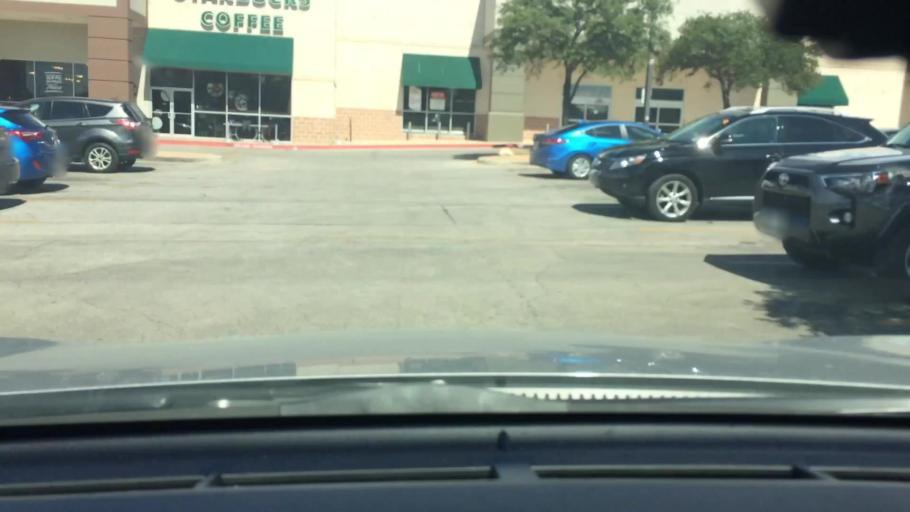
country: US
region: Texas
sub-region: Bexar County
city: Shavano Park
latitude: 29.5611
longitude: -98.5886
